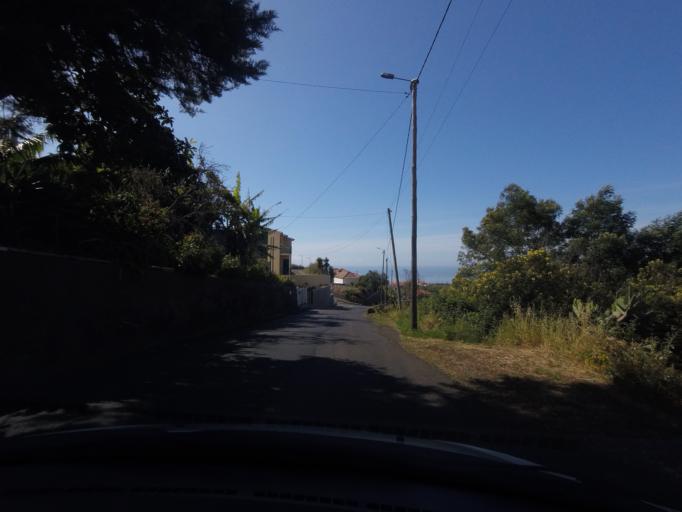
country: PT
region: Madeira
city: Canico
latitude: 32.6547
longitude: -16.8550
